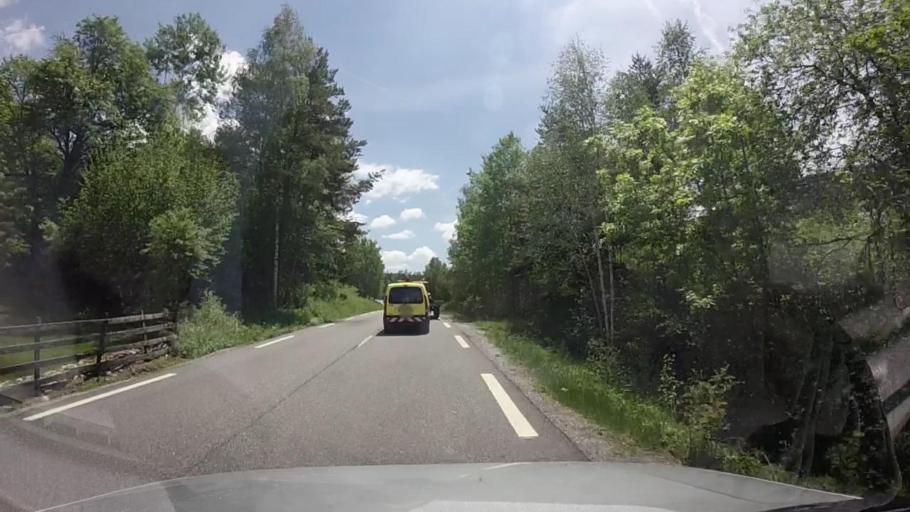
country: FR
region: Provence-Alpes-Cote d'Azur
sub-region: Departement des Alpes-de-Haute-Provence
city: Seyne-les-Alpes
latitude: 44.3286
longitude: 6.3917
